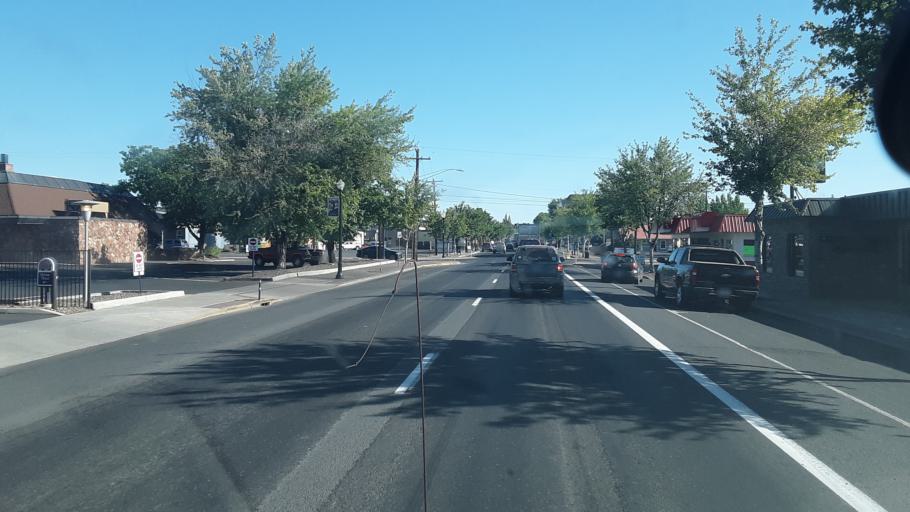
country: US
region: Oregon
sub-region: Jefferson County
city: Madras
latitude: 44.6353
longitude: -121.1306
